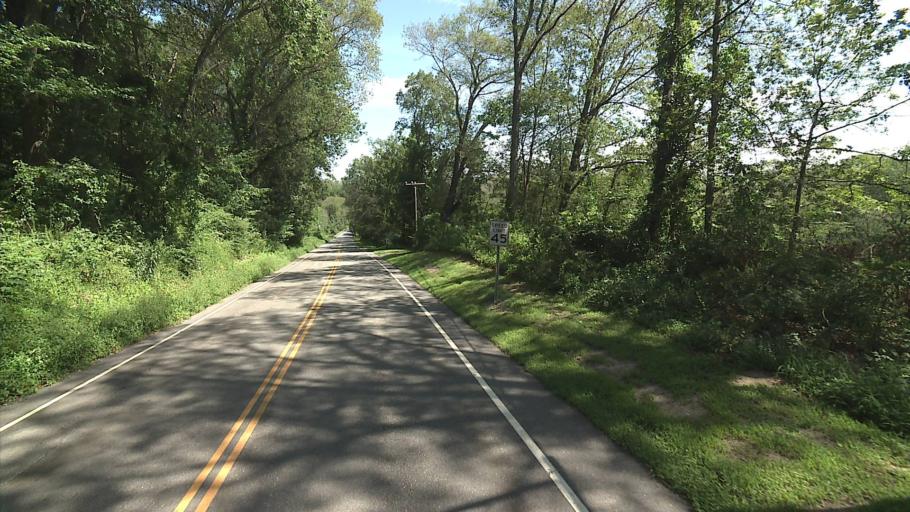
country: US
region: Connecticut
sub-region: Windham County
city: South Woodstock
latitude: 41.8287
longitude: -72.0247
